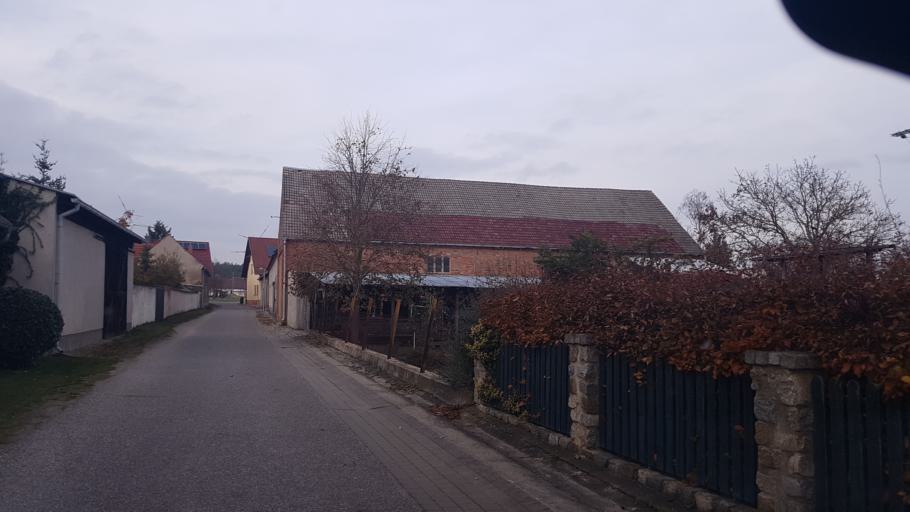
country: DE
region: Brandenburg
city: Schilda
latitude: 51.6459
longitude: 13.3929
